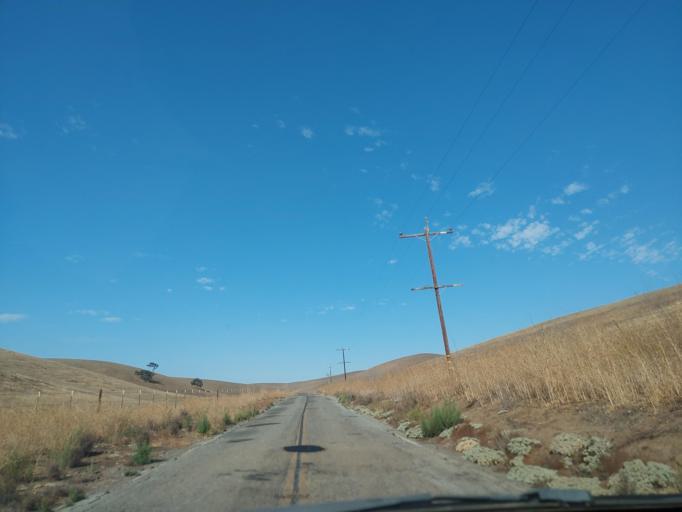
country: US
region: California
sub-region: San Benito County
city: Ridgemark
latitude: 36.7998
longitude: -121.2790
